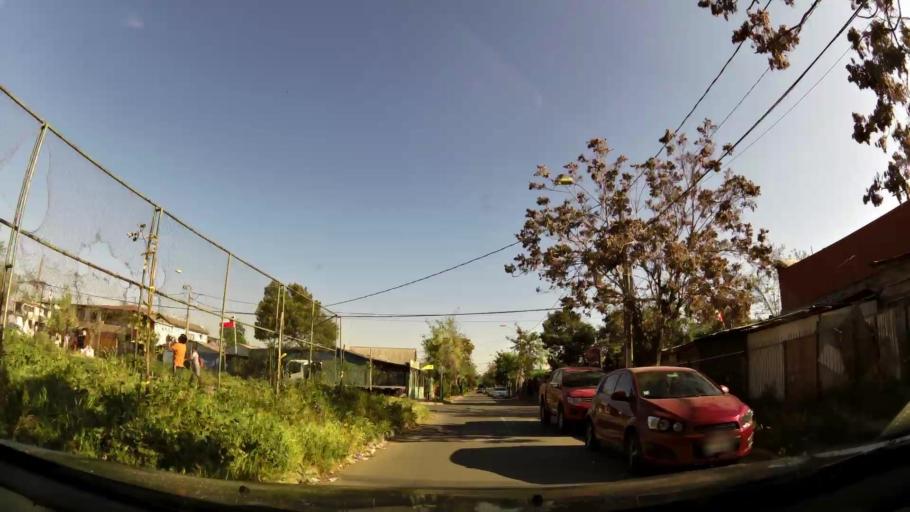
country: CL
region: Santiago Metropolitan
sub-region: Provincia de Santiago
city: La Pintana
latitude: -33.5807
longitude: -70.6561
